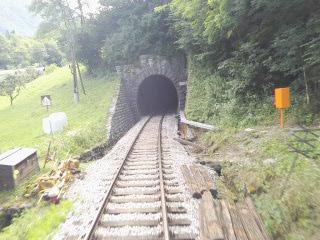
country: SI
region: Tolmin
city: Tolmin
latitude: 46.1594
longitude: 13.8293
